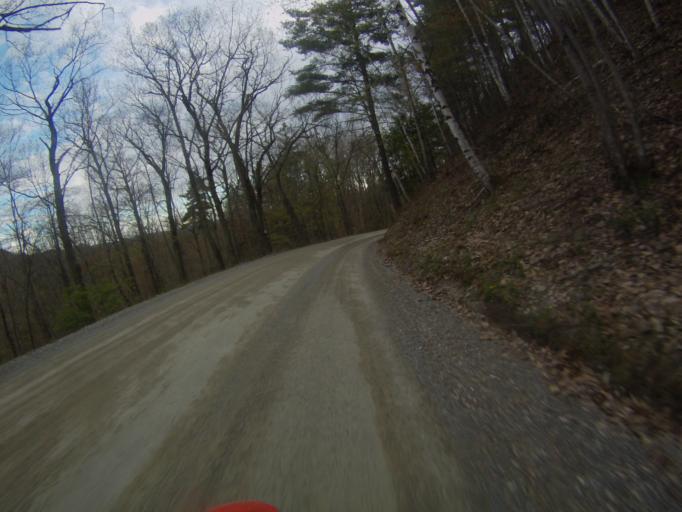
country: US
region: Vermont
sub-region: Addison County
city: Middlebury (village)
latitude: 43.9752
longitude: -73.0739
